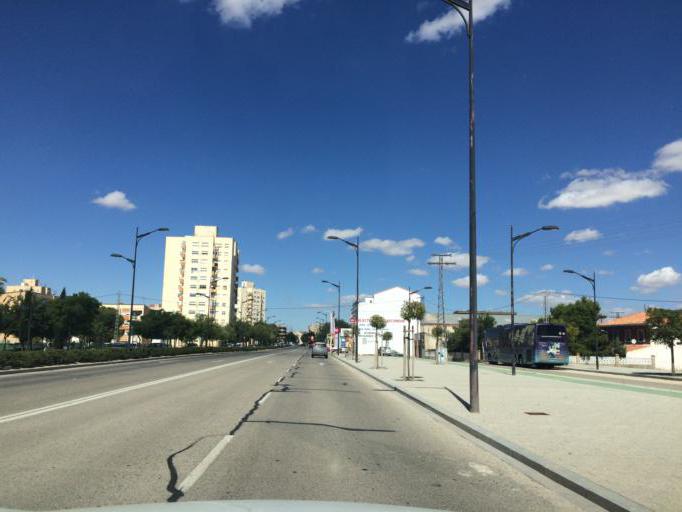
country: ES
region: Castille-La Mancha
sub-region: Provincia de Albacete
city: Albacete
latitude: 38.9805
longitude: -1.8468
